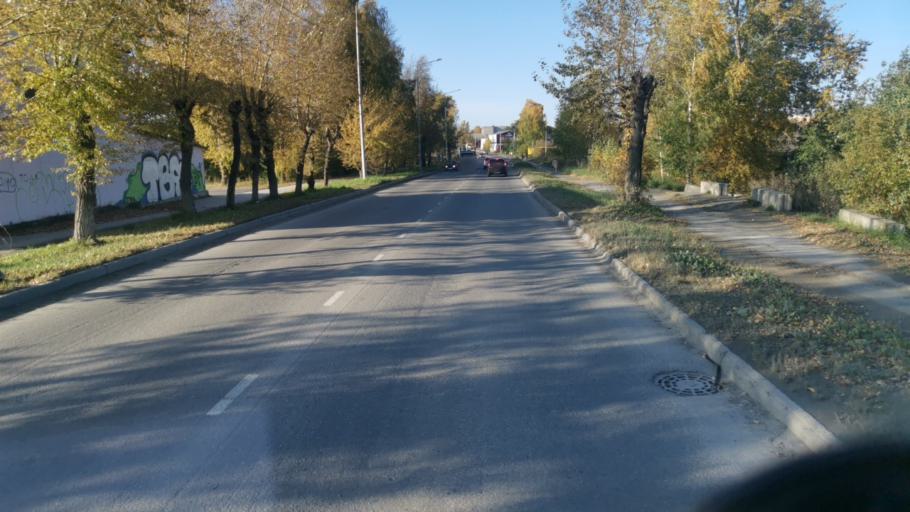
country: RU
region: Sverdlovsk
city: Nizhniy Tagil
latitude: 57.9288
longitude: 59.9360
